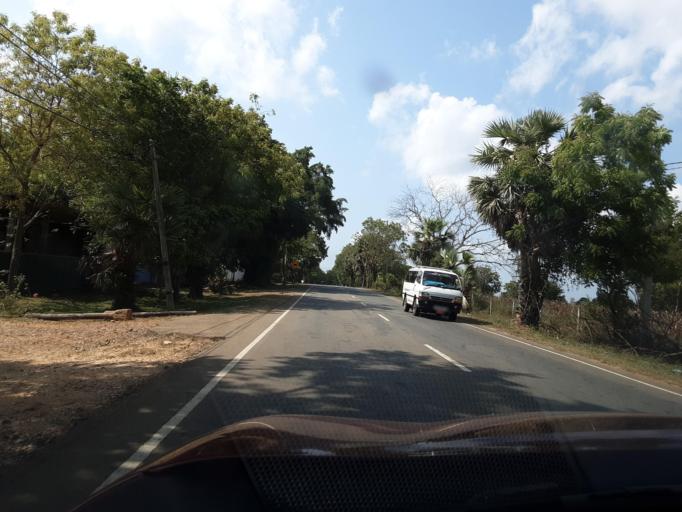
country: LK
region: Southern
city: Tangalla
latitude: 6.2610
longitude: 81.2262
